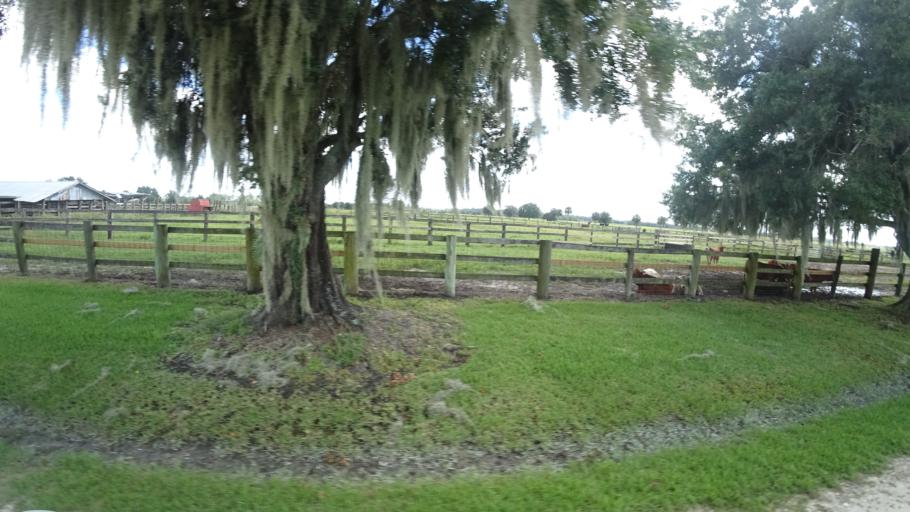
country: US
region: Florida
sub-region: Sarasota County
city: Warm Mineral Springs
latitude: 27.2540
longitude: -82.1622
